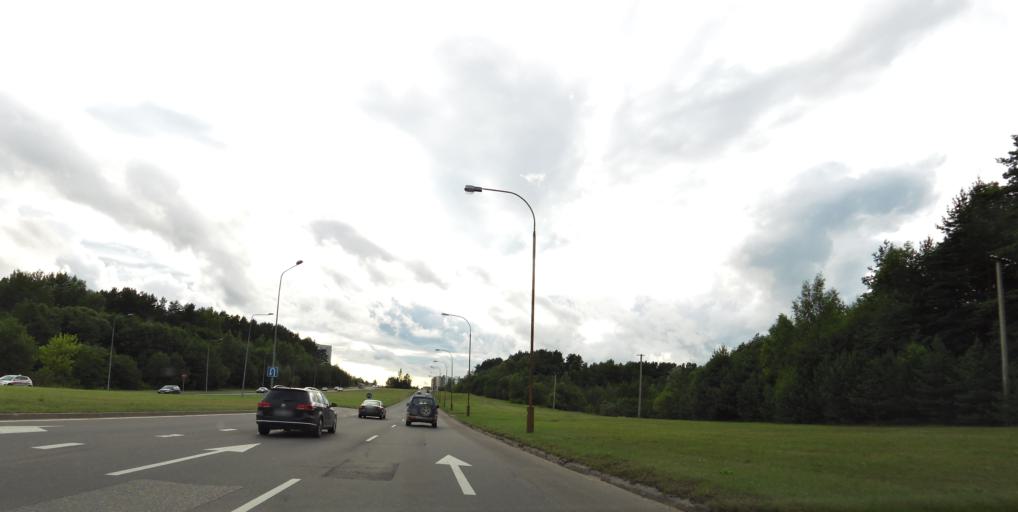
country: LT
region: Vilnius County
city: Pilaite
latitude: 54.7065
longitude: 25.1964
